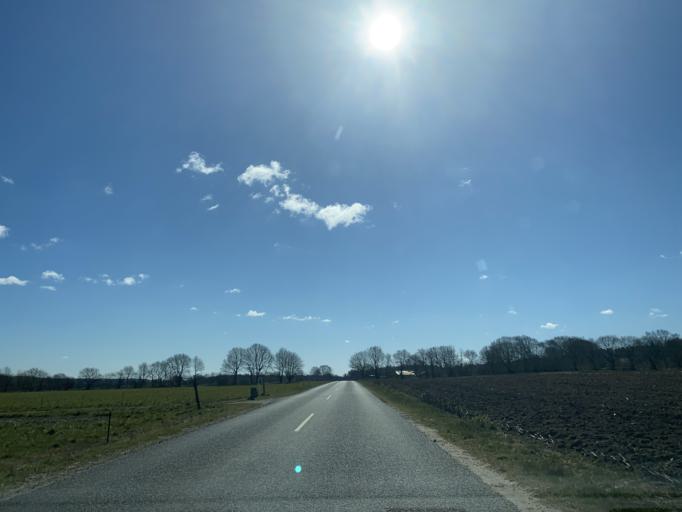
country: DK
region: Central Jutland
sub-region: Viborg Kommune
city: Bjerringbro
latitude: 56.2581
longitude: 9.6452
